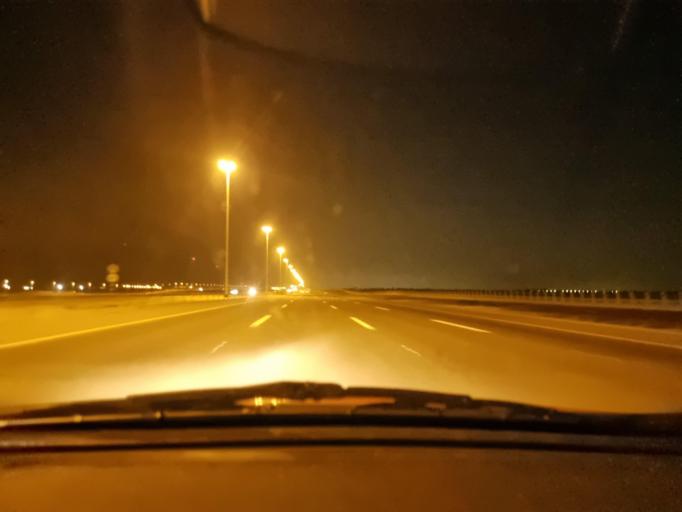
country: AE
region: Abu Dhabi
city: Abu Dhabi
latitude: 24.5366
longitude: 54.7466
